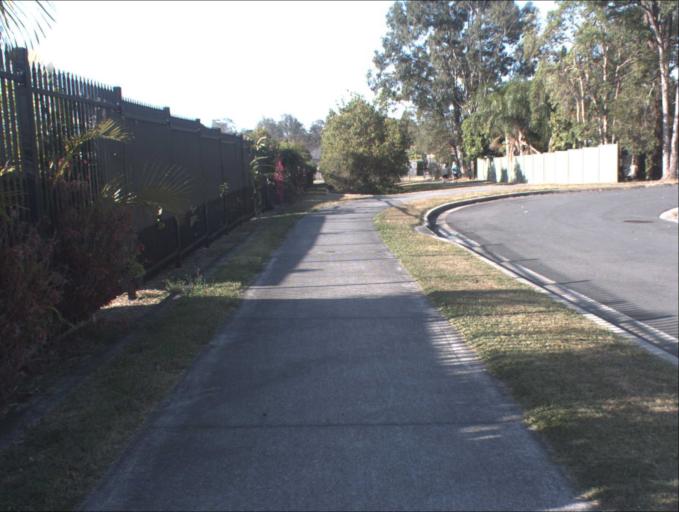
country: AU
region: Queensland
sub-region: Gold Coast
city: Yatala
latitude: -27.7084
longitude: 153.2203
